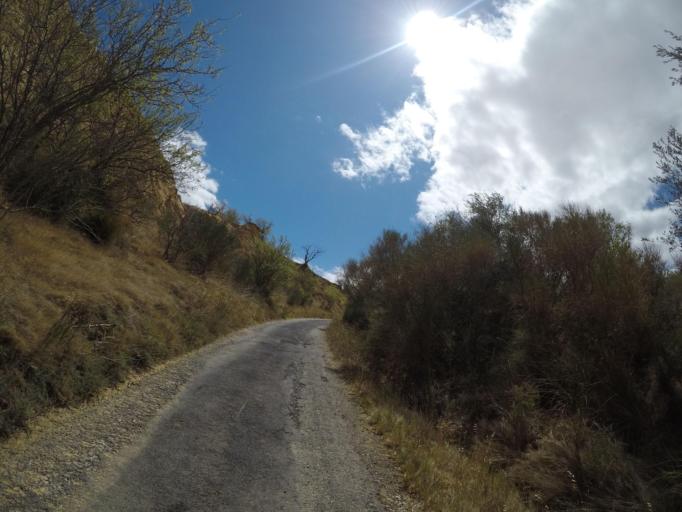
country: FR
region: Languedoc-Roussillon
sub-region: Departement des Pyrenees-Orientales
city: Baixas
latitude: 42.7436
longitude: 2.8067
